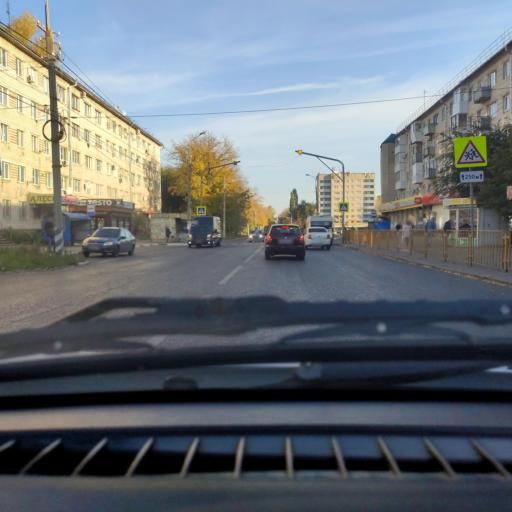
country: RU
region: Samara
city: Tol'yatti
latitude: 53.5141
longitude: 49.4233
